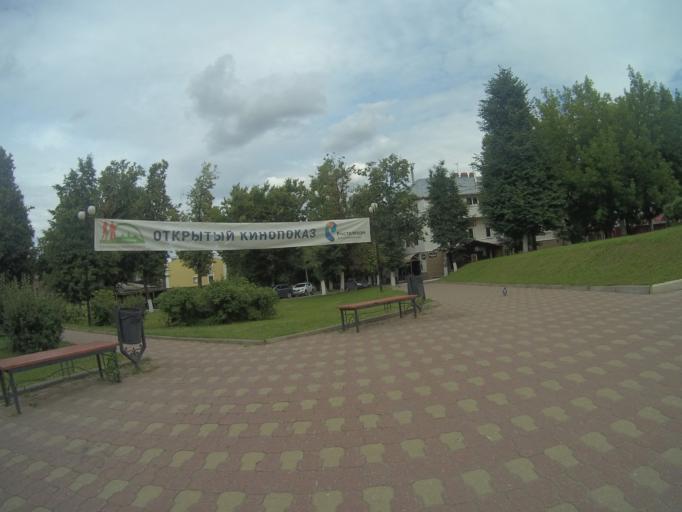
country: RU
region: Vladimir
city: Vladimir
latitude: 56.1280
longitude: 40.3969
